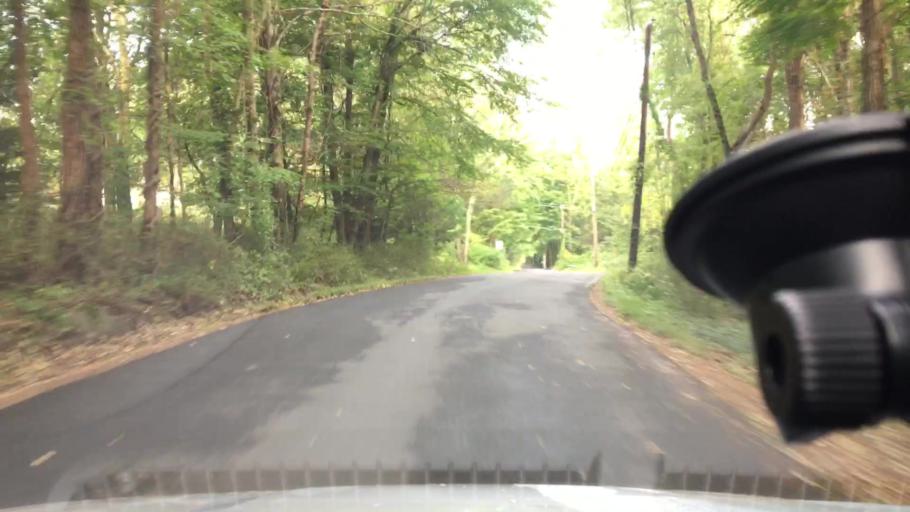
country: US
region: Pennsylvania
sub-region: Monroe County
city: Mountainhome
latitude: 41.1627
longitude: -75.2660
